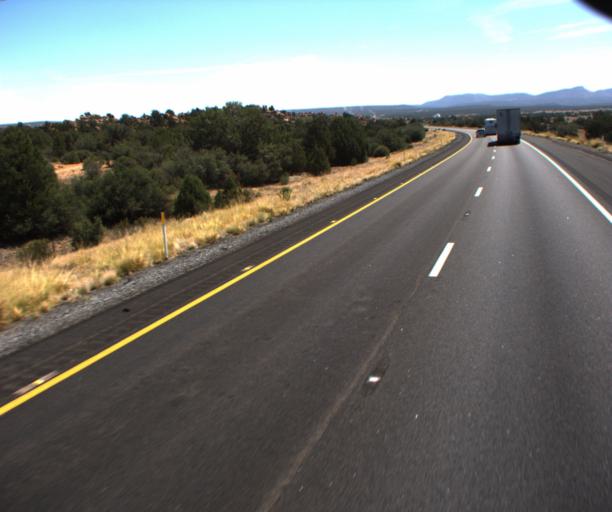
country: US
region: Arizona
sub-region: Mohave County
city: Peach Springs
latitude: 35.1833
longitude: -113.3910
